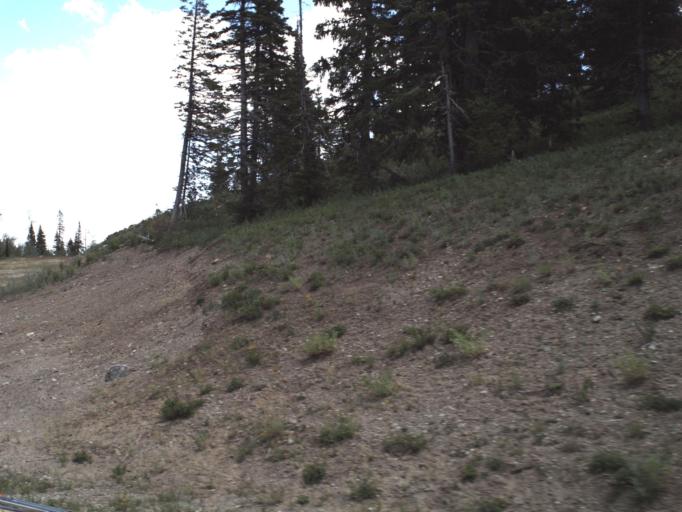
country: US
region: Utah
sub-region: Weber County
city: Wolf Creek
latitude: 41.4648
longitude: -111.4961
